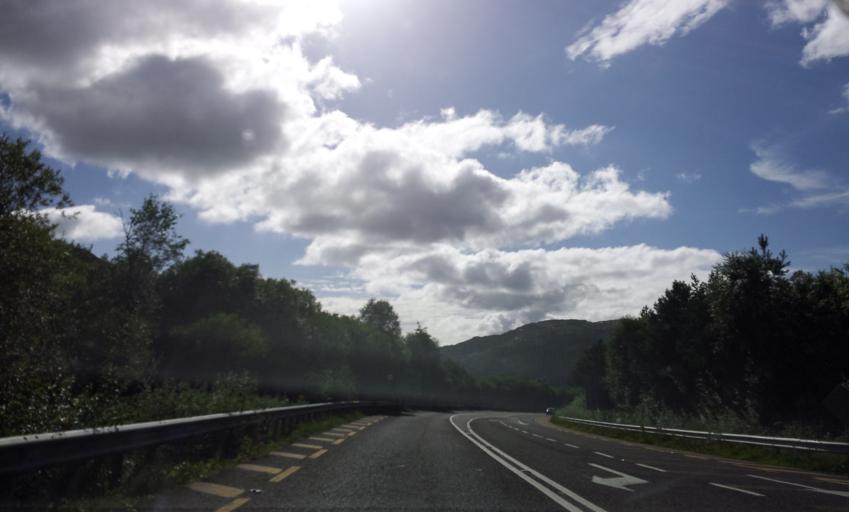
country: IE
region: Munster
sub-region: Ciarrai
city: Cill Airne
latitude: 51.9819
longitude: -9.3148
